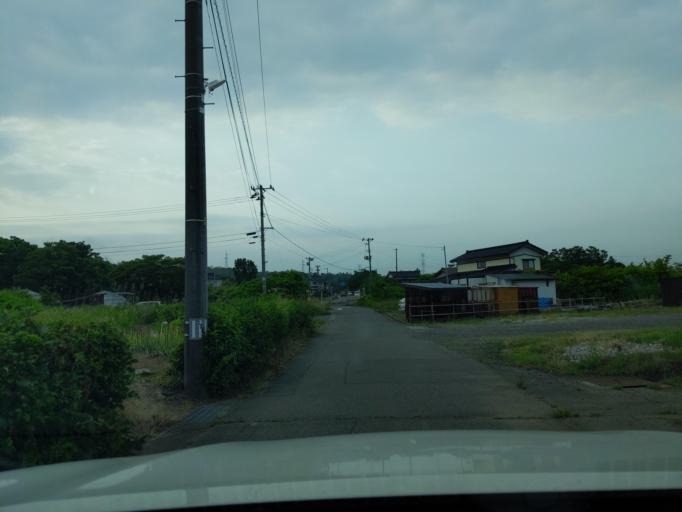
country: JP
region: Niigata
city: Kashiwazaki
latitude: 37.4017
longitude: 138.6001
